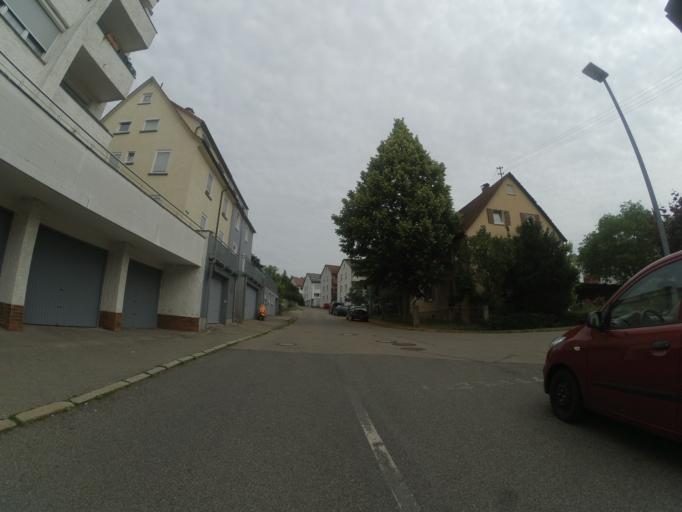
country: DE
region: Baden-Wuerttemberg
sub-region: Tuebingen Region
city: Dornstadt
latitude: 48.4157
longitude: 9.9224
